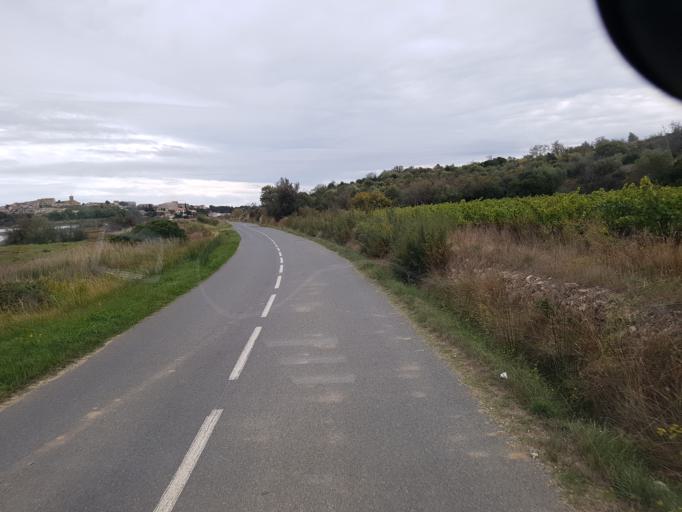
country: FR
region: Languedoc-Roussillon
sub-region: Departement de l'Aude
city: Peyriac-de-Mer
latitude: 43.1308
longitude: 2.9860
